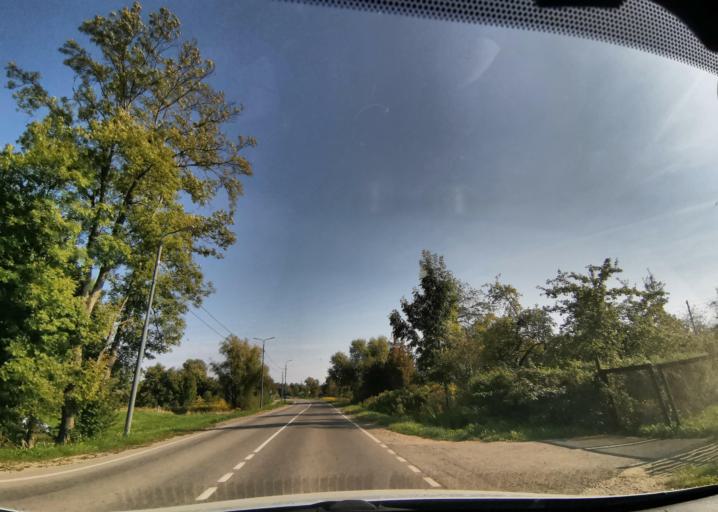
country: RU
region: Kaliningrad
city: Neman
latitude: 55.0271
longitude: 22.0540
